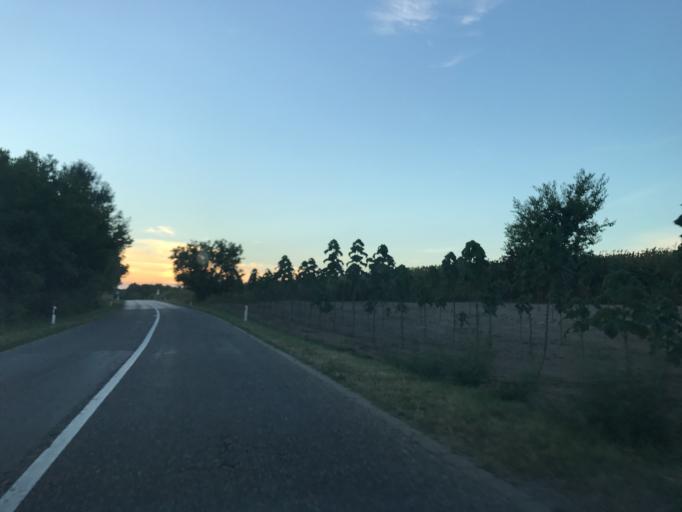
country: RS
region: Central Serbia
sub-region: Branicevski Okrug
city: Veliko Gradiste
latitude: 44.7115
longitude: 21.5221
